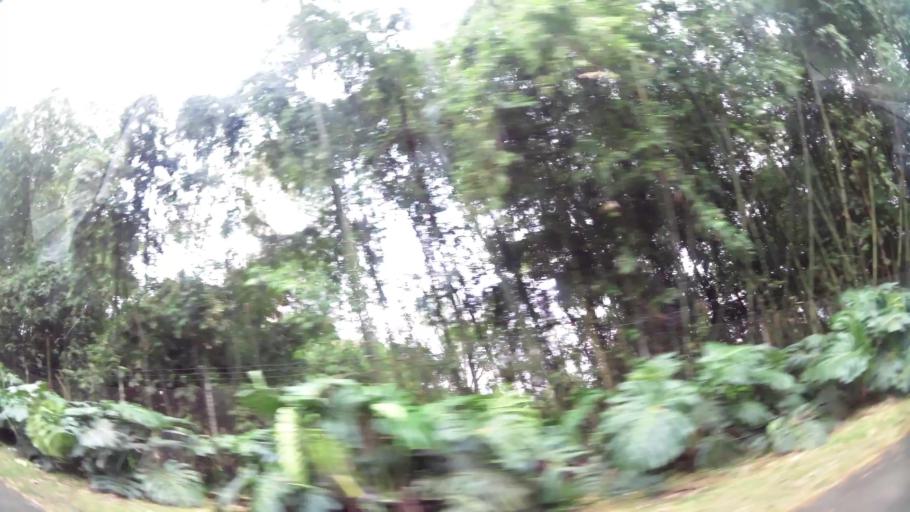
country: CO
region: Antioquia
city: Envigado
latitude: 6.1916
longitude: -75.5548
